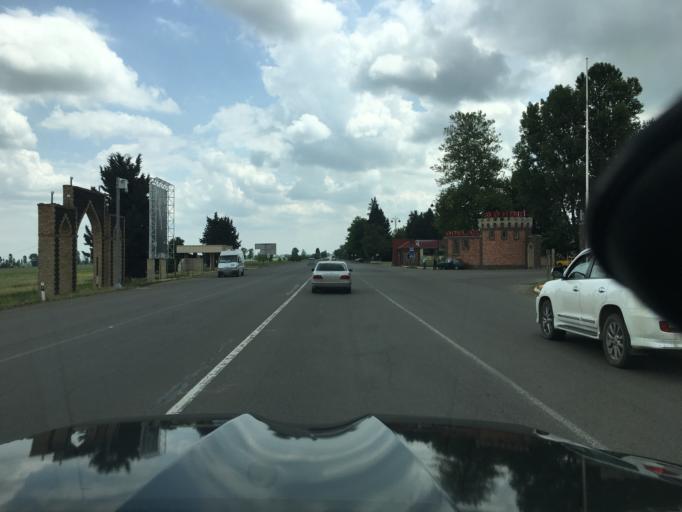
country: AZ
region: Tovuz
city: Tovuz
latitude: 40.9596
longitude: 45.7241
